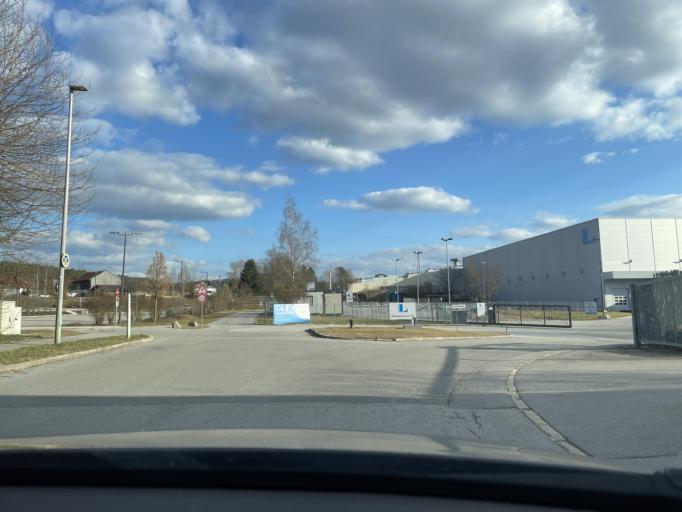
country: DE
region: Bavaria
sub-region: Lower Bavaria
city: Viechtach
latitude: 49.0657
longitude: 12.8885
